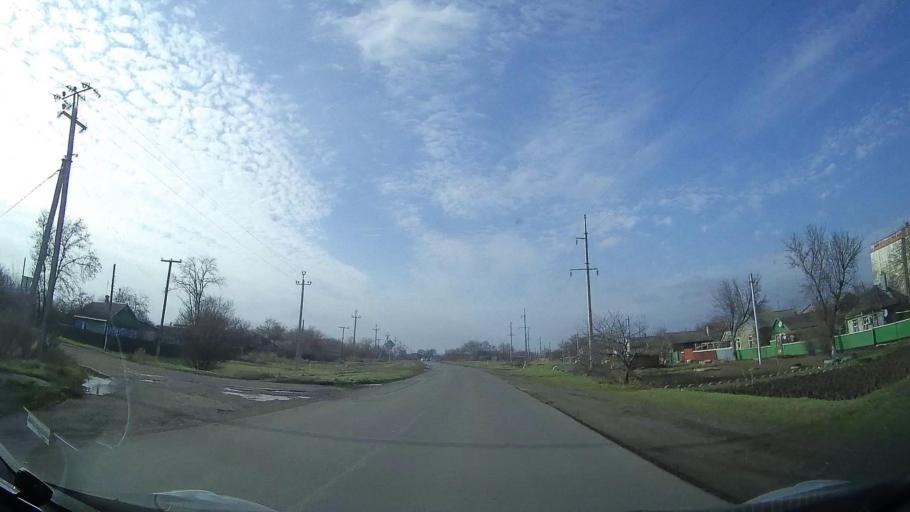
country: RU
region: Rostov
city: Mechetinskaya
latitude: 46.7867
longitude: 40.4768
